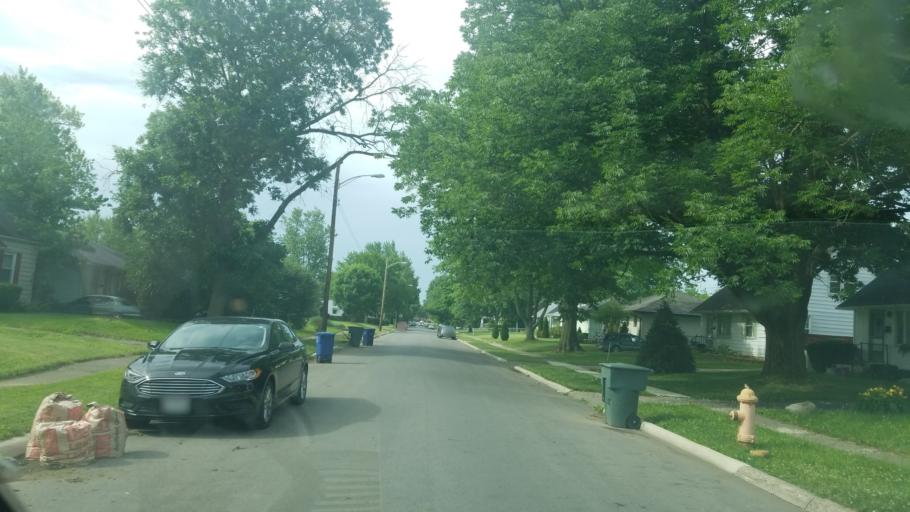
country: US
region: Ohio
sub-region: Franklin County
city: Minerva Park
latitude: 40.0395
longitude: -82.9687
